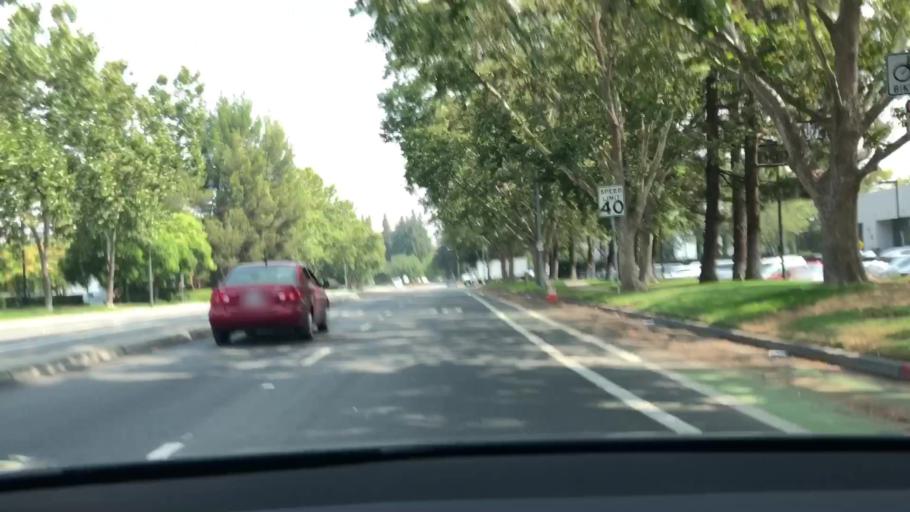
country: US
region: California
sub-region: Santa Clara County
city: Seven Trees
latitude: 37.2355
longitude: -121.7774
